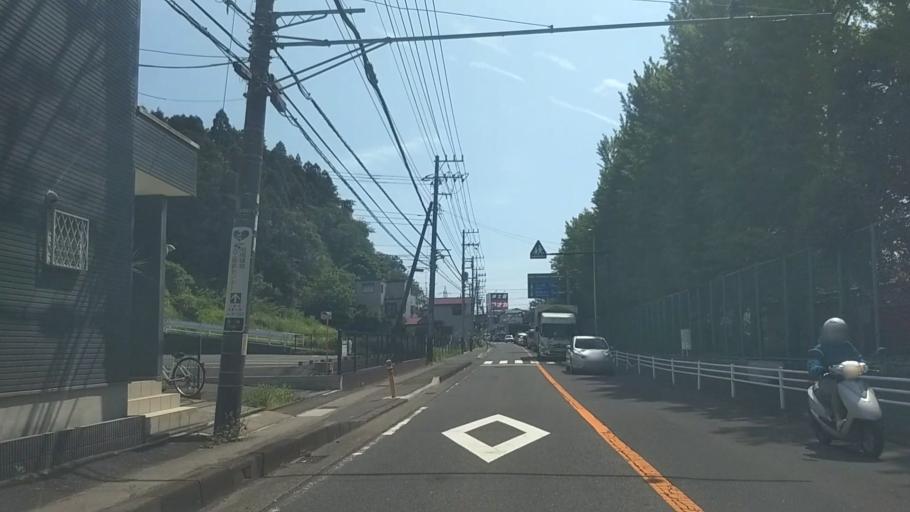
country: JP
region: Kanagawa
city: Kamakura
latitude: 35.3592
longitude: 139.5471
